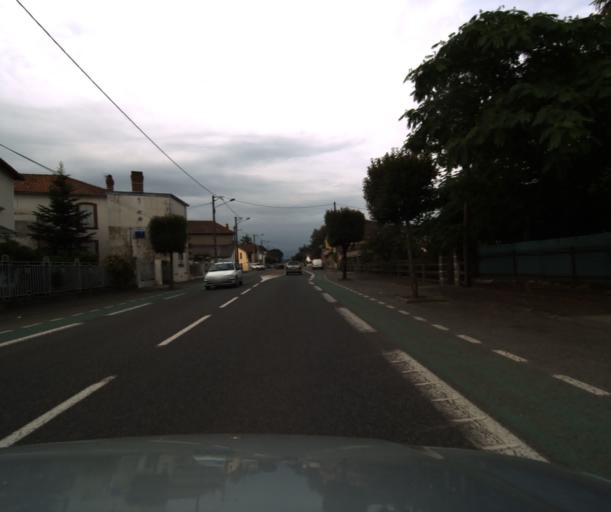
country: FR
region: Midi-Pyrenees
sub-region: Departement des Hautes-Pyrenees
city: Aureilhan
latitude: 43.2405
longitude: 0.0946
